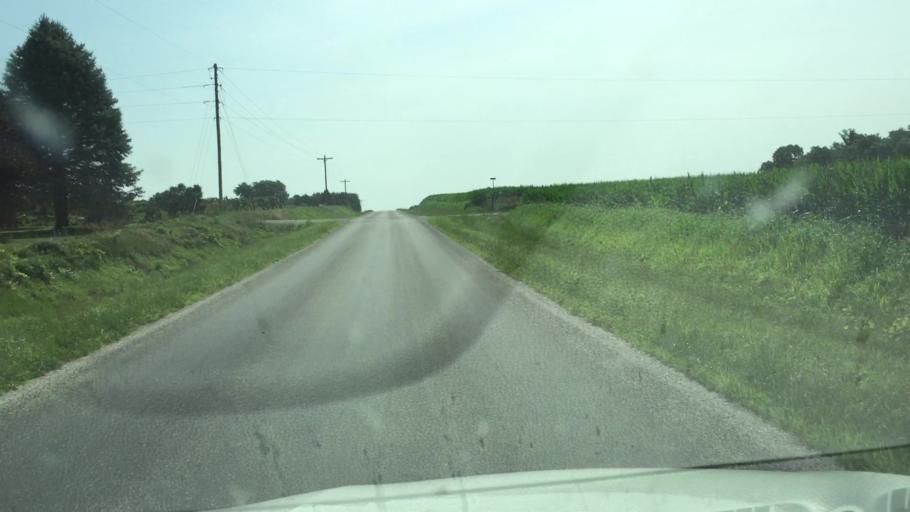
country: US
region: Illinois
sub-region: Hancock County
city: Nauvoo
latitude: 40.5114
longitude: -91.3476
